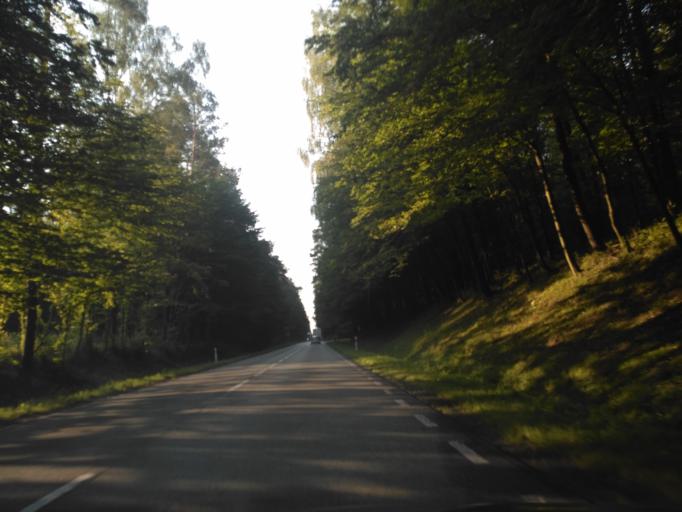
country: PL
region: Lublin Voivodeship
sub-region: Powiat krasnicki
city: Szastarka
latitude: 50.8536
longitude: 22.2863
